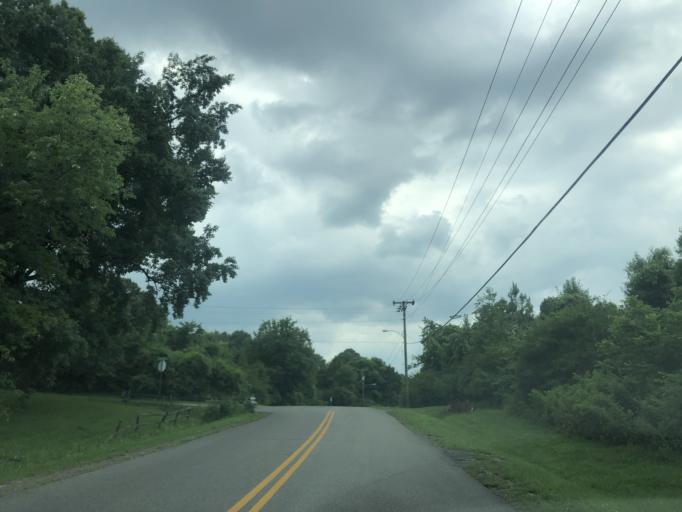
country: US
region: Tennessee
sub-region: Davidson County
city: Oak Hill
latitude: 36.1012
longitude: -86.6679
